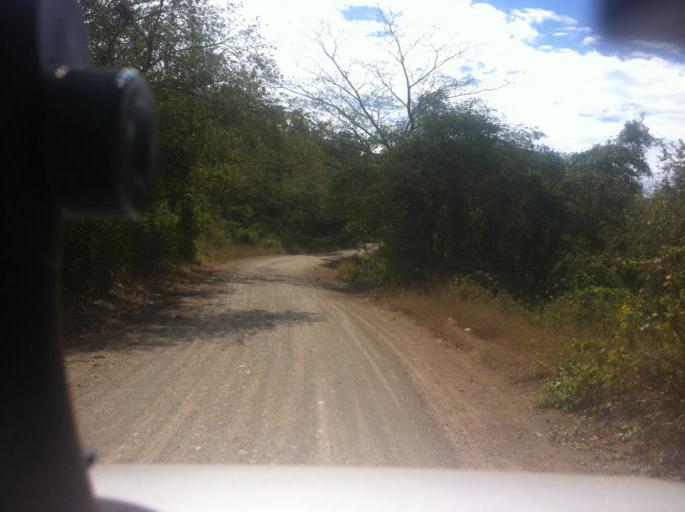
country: NI
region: Rivas
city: Belen
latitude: 11.5661
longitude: -86.0285
